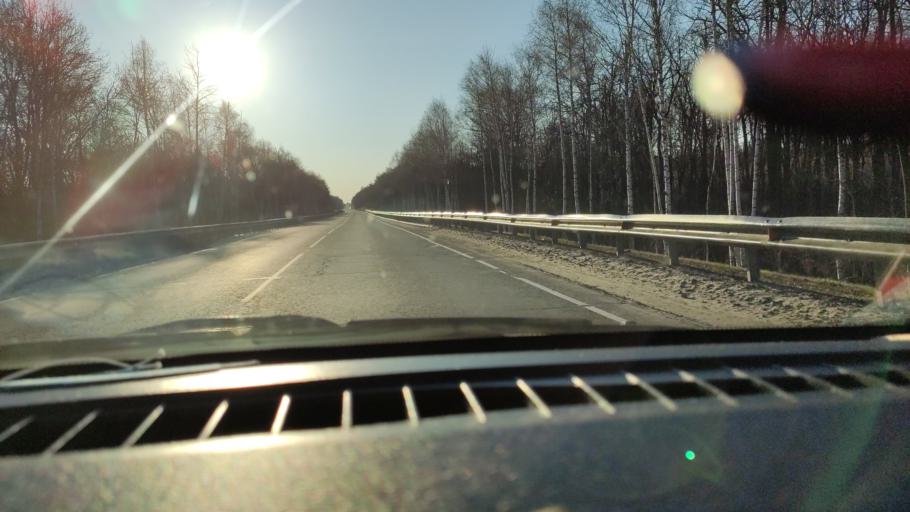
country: RU
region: Saratov
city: Vol'sk
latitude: 52.1117
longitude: 47.3328
